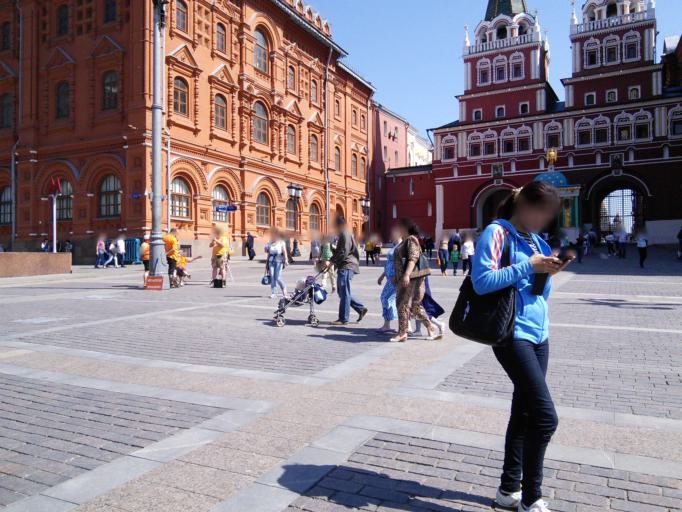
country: RU
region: Moscow
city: Moscow
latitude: 55.7560
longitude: 37.6172
